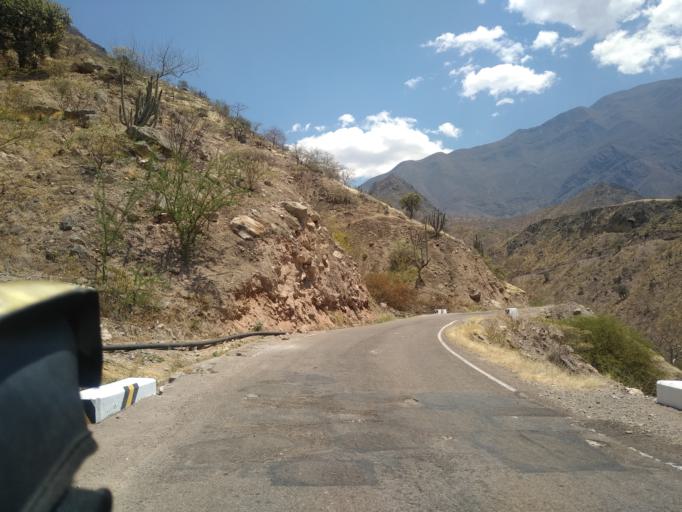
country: PE
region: Amazonas
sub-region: Provincia de Chachapoyas
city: Balsas
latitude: -6.8521
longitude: -78.0360
